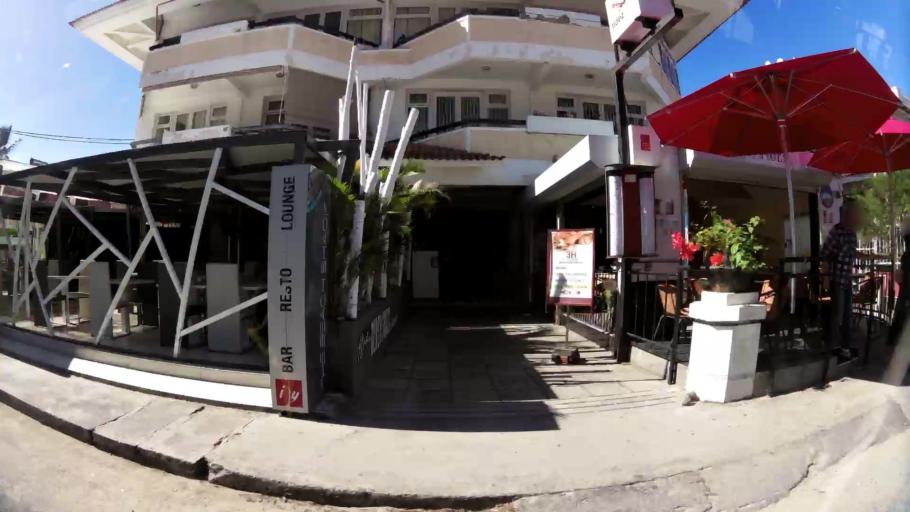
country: MU
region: Black River
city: Flic en Flac
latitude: -20.2851
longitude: 57.3644
